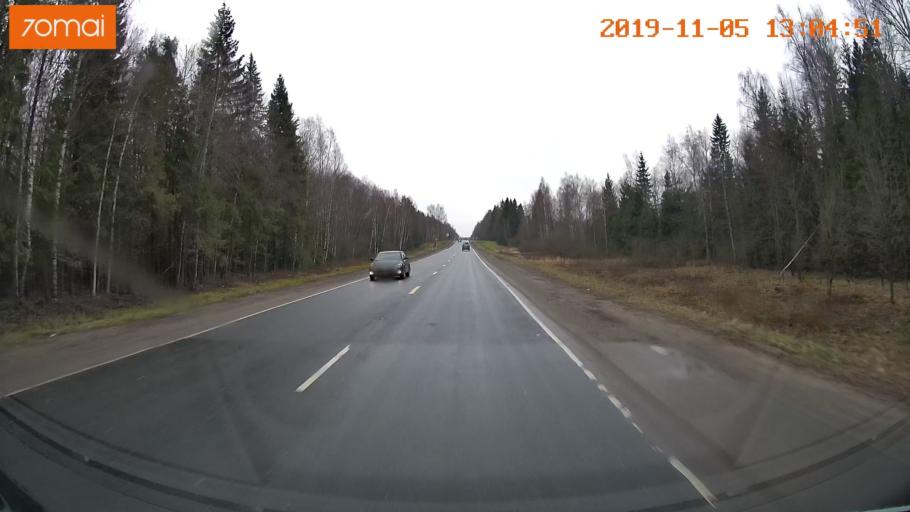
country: RU
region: Ivanovo
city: Kitovo
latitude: 56.8863
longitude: 41.2303
